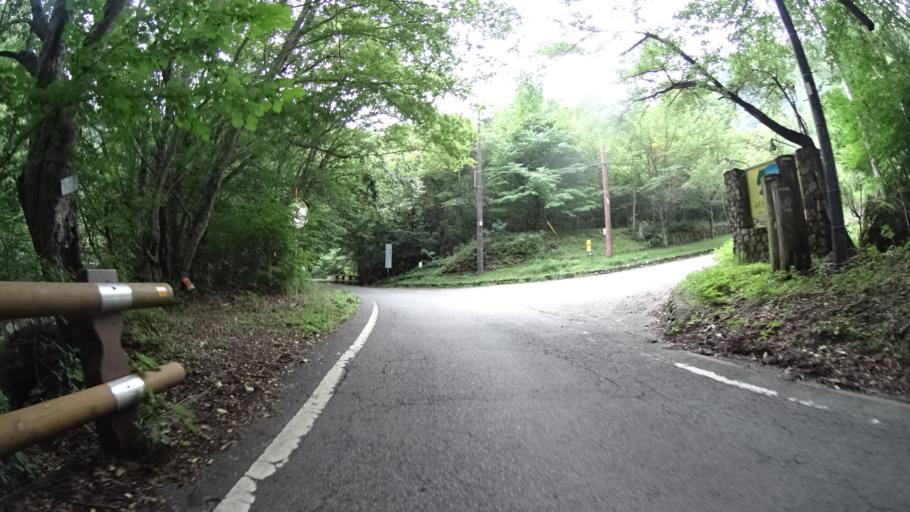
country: JP
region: Yamanashi
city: Kofu-shi
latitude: 35.8585
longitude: 138.5635
